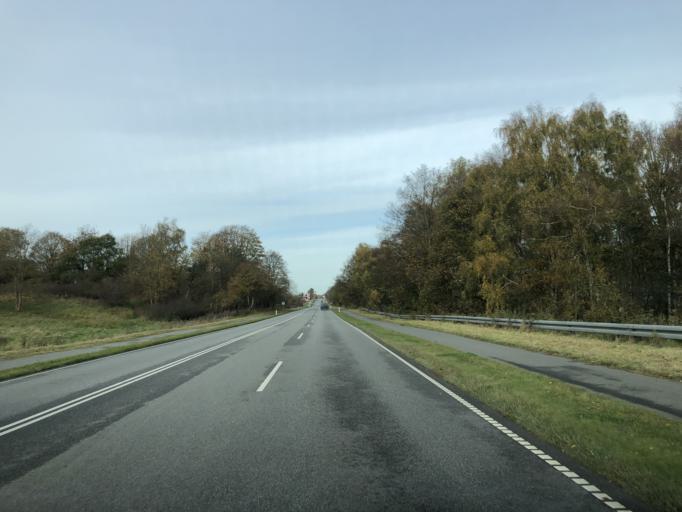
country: DK
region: Capital Region
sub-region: Allerod Kommune
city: Blovstrod
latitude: 55.8600
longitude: 12.3976
